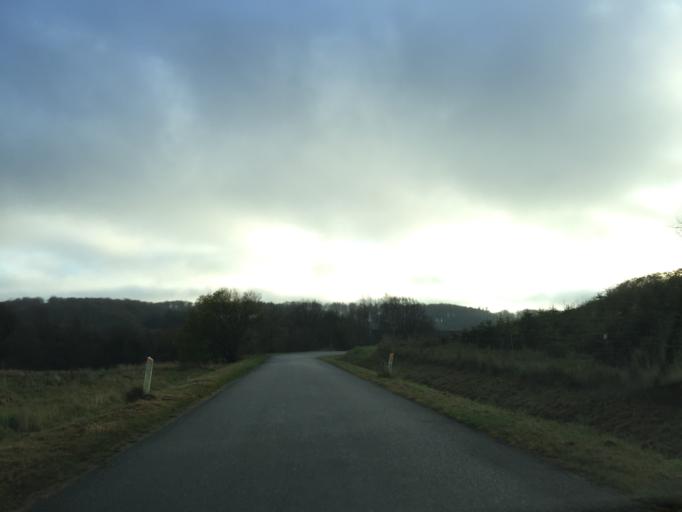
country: DK
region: Central Jutland
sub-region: Skanderborg Kommune
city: Ry
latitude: 56.1667
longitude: 9.7741
